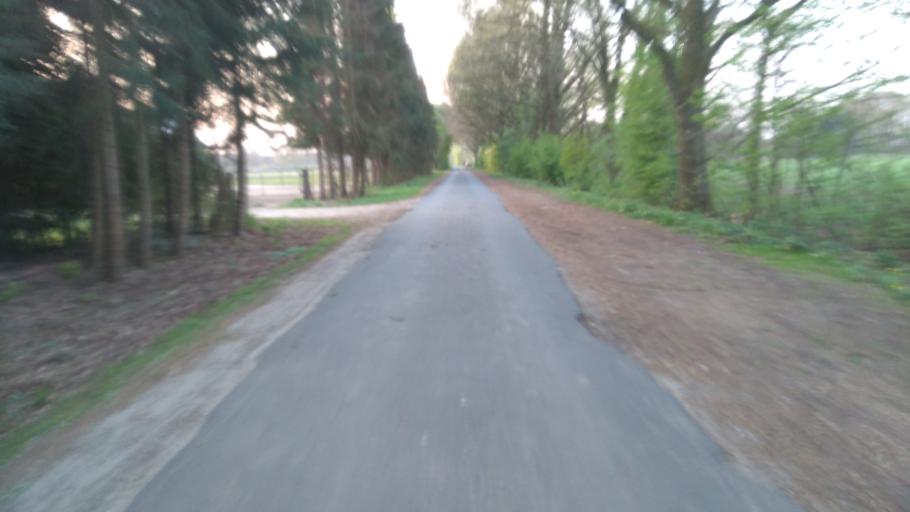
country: DE
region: Lower Saxony
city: Harsefeld
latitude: 53.4891
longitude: 9.5138
